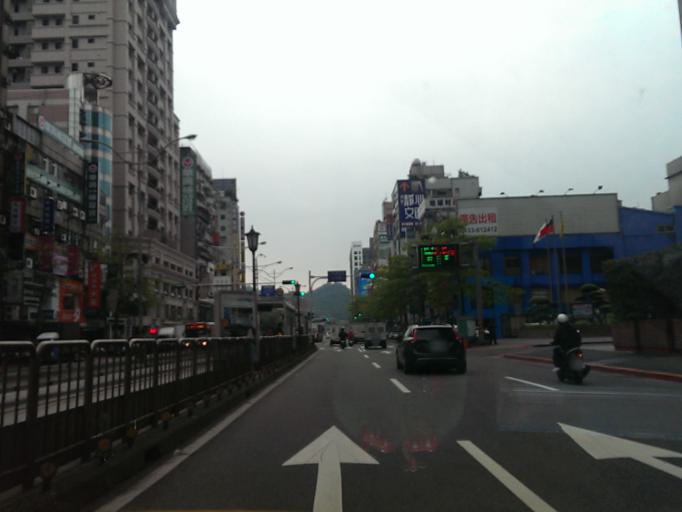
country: TW
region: Taipei
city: Taipei
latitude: 25.0178
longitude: 121.5311
